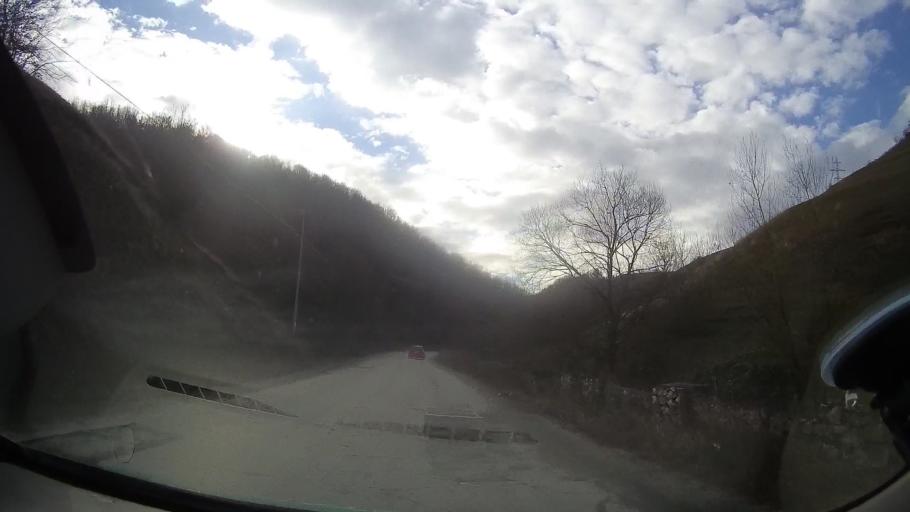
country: RO
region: Cluj
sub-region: Comuna Baisoara
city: Baisoara
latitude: 46.5930
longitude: 23.4601
